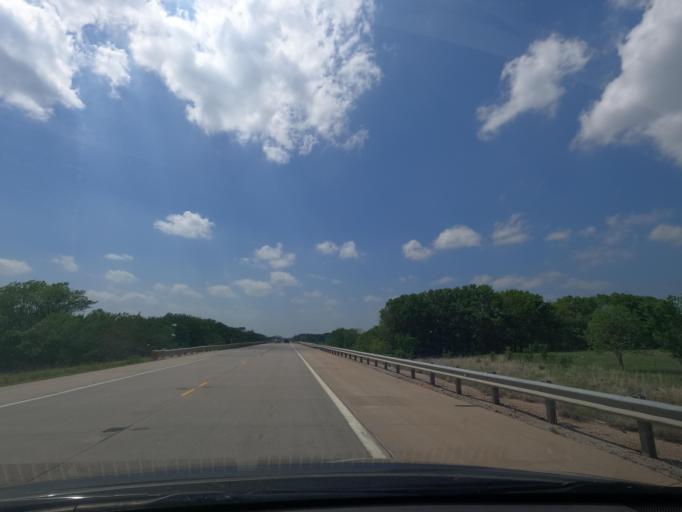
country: US
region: Kansas
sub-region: Wilson County
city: Fredonia
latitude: 37.6202
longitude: -96.0388
